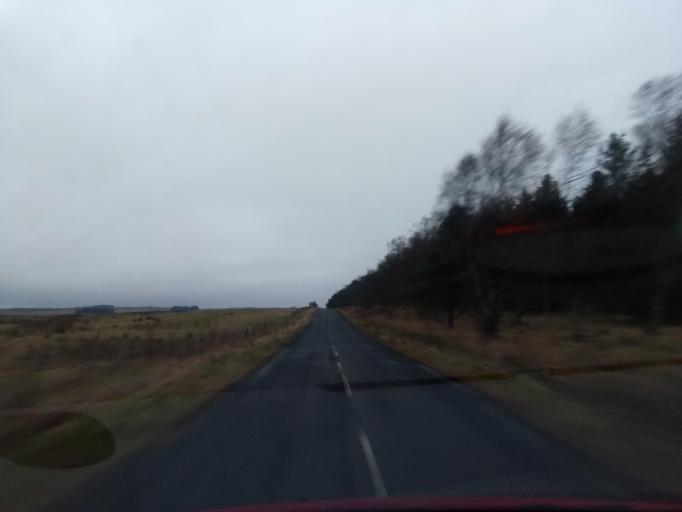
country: GB
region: England
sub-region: Northumberland
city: Rothley
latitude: 55.2015
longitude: -1.9917
